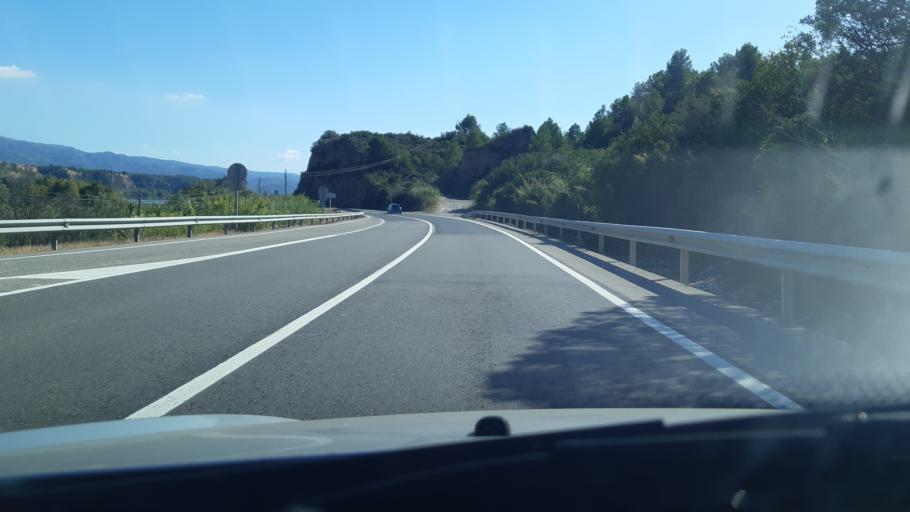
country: ES
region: Catalonia
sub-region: Provincia de Tarragona
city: Tivenys
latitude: 40.8989
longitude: 0.4848
